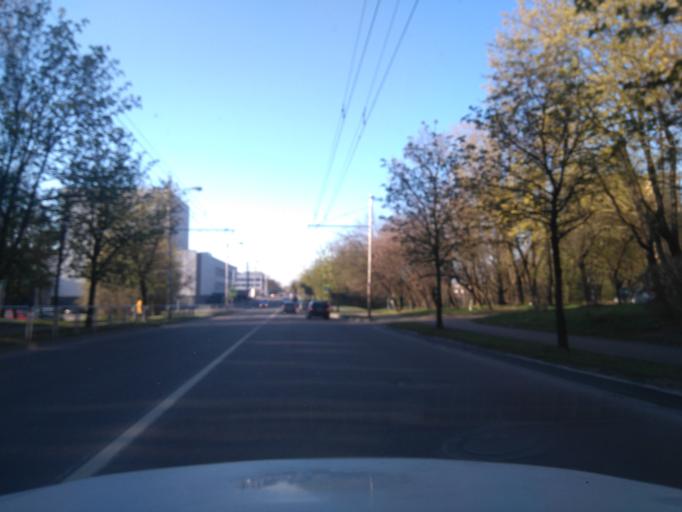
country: LT
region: Kauno apskritis
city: Dainava (Kaunas)
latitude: 54.9083
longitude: 23.9738
